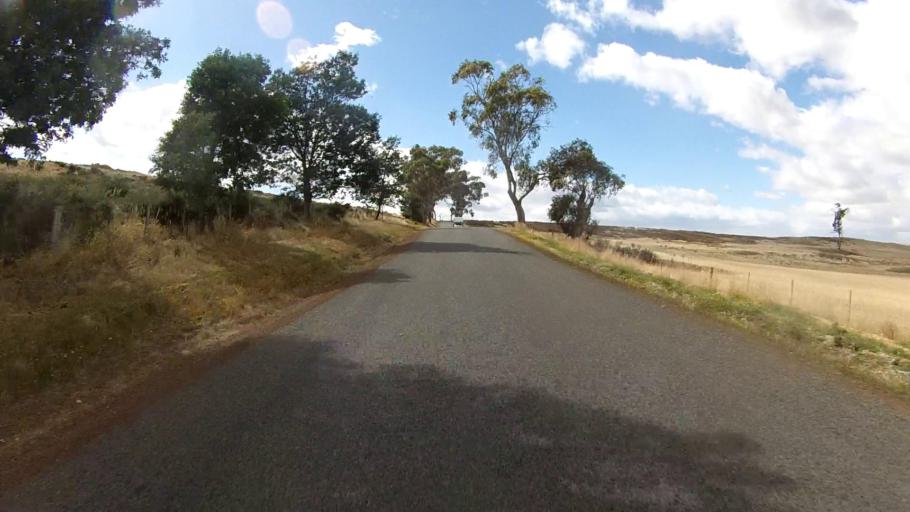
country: AU
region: Tasmania
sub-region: Northern Midlands
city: Evandale
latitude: -41.7049
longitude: 147.3889
